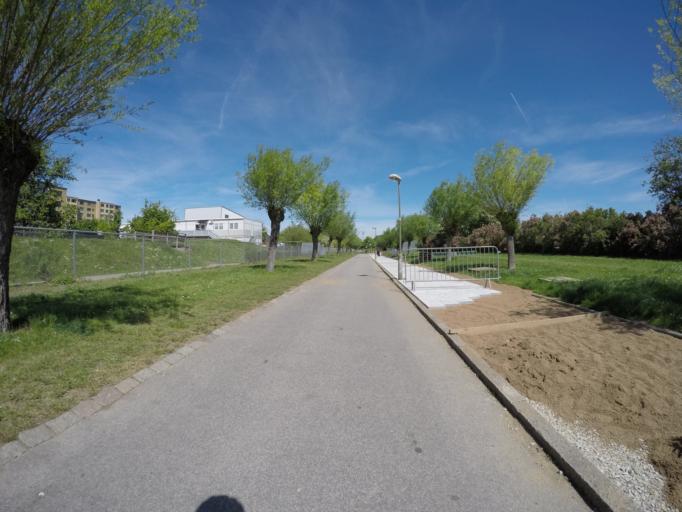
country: SE
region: Skane
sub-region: Malmo
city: Malmoe
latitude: 55.5803
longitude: 12.9827
